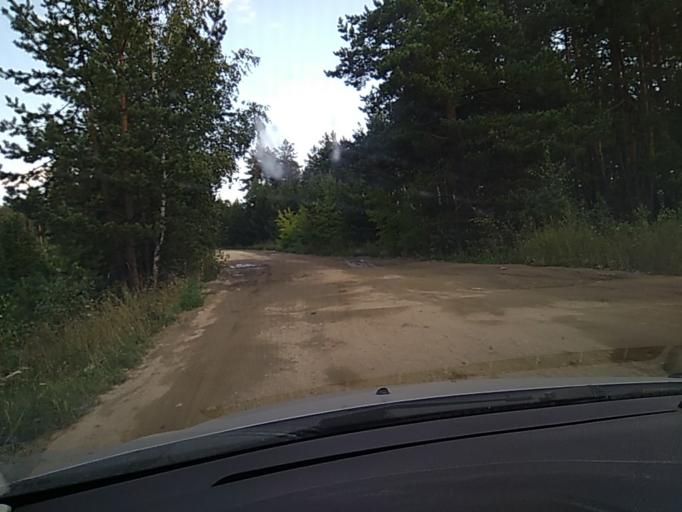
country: RU
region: Chelyabinsk
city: Kyshtym
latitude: 55.6849
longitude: 60.5691
